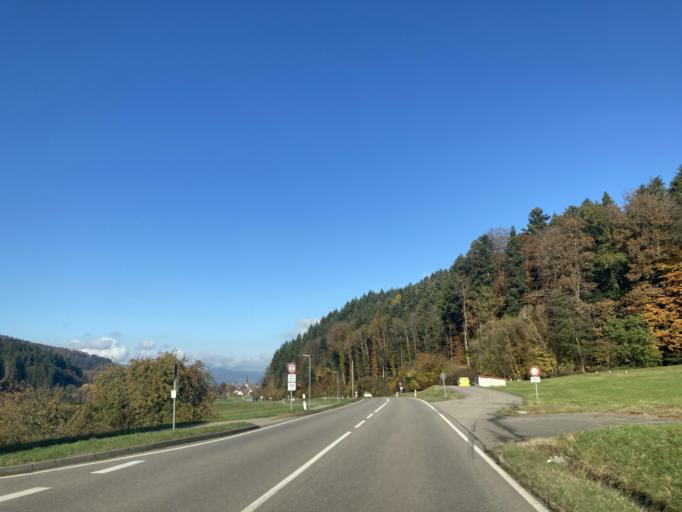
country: DE
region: Baden-Wuerttemberg
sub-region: Freiburg Region
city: Muhlenbach
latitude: 48.2618
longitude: 8.1026
